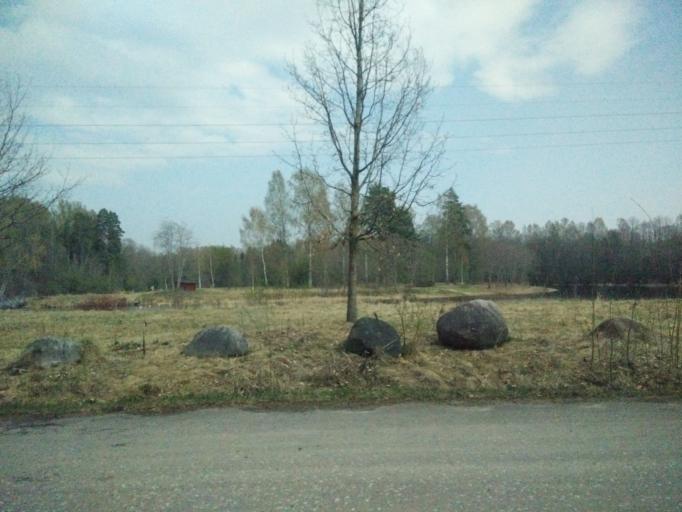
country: SE
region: Vaermland
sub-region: Munkfors Kommun
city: Munkfors
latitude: 59.8462
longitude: 13.5472
